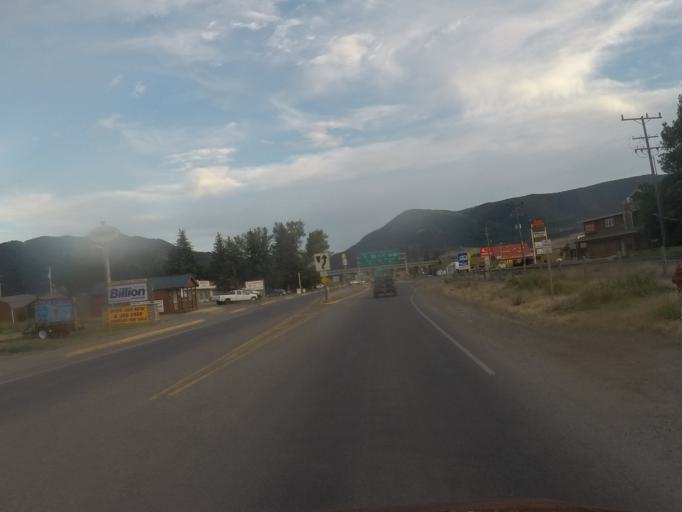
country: US
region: Montana
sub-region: Park County
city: Livingston
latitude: 45.6479
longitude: -110.5729
